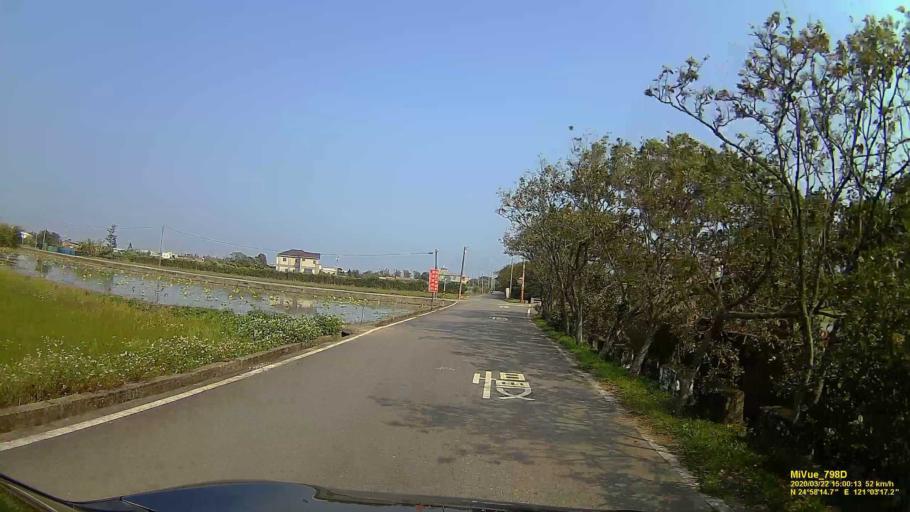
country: TW
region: Taiwan
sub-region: Hsinchu
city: Zhubei
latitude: 24.9706
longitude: 121.0550
